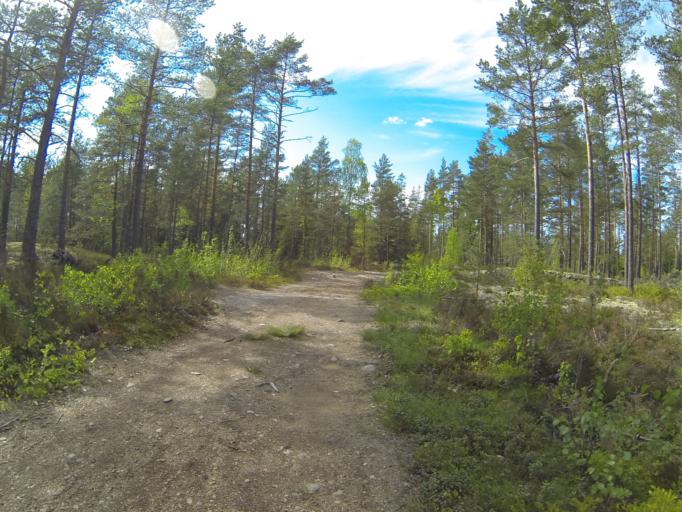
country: FI
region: Varsinais-Suomi
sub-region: Salo
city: Salo
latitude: 60.3900
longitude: 23.1934
